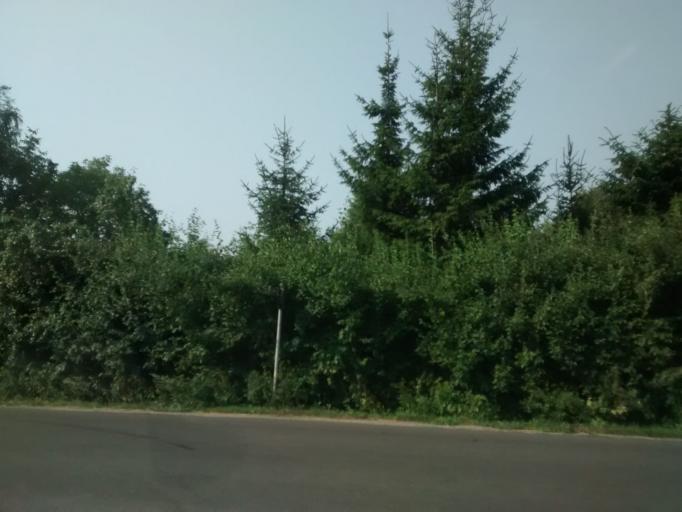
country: PL
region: Silesian Voivodeship
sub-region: Powiat zawiercianski
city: Wlodowice
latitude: 50.6263
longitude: 19.5061
